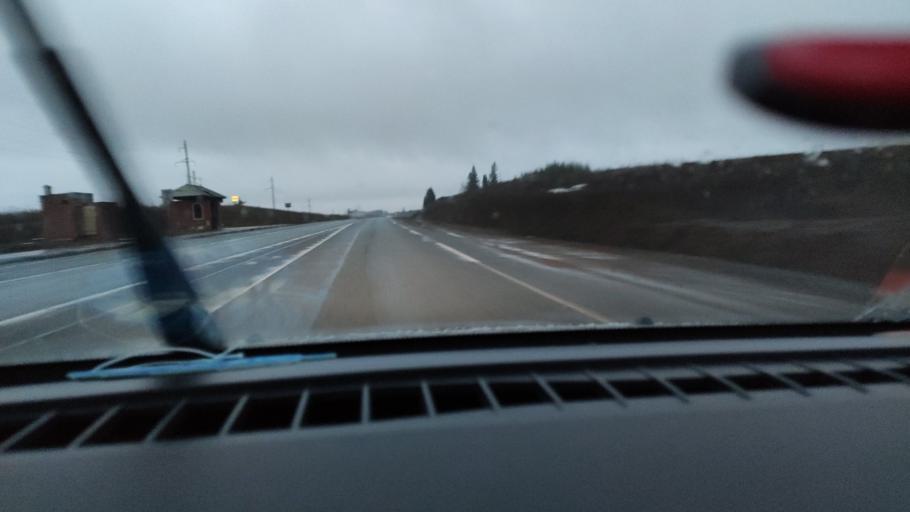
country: RU
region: Udmurtiya
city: Alnashi
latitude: 56.2312
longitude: 52.4056
